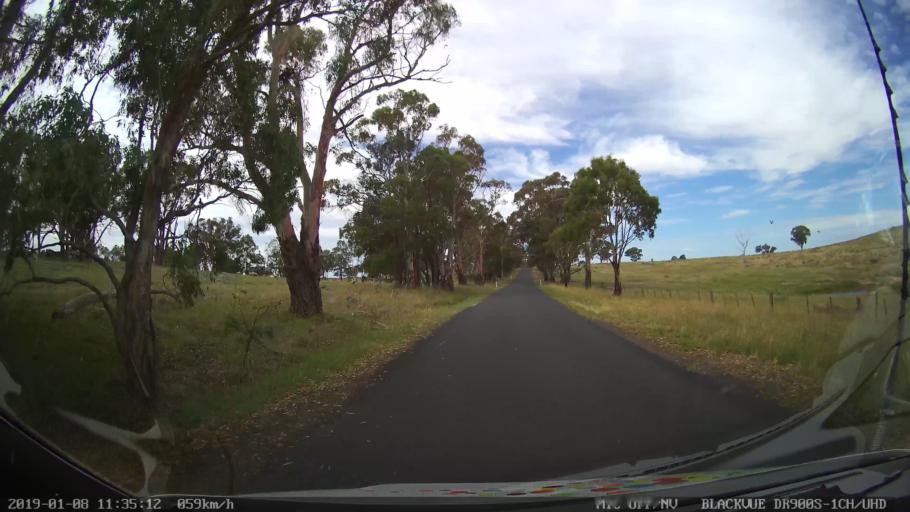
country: AU
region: New South Wales
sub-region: Guyra
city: Guyra
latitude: -30.3349
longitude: 151.5378
